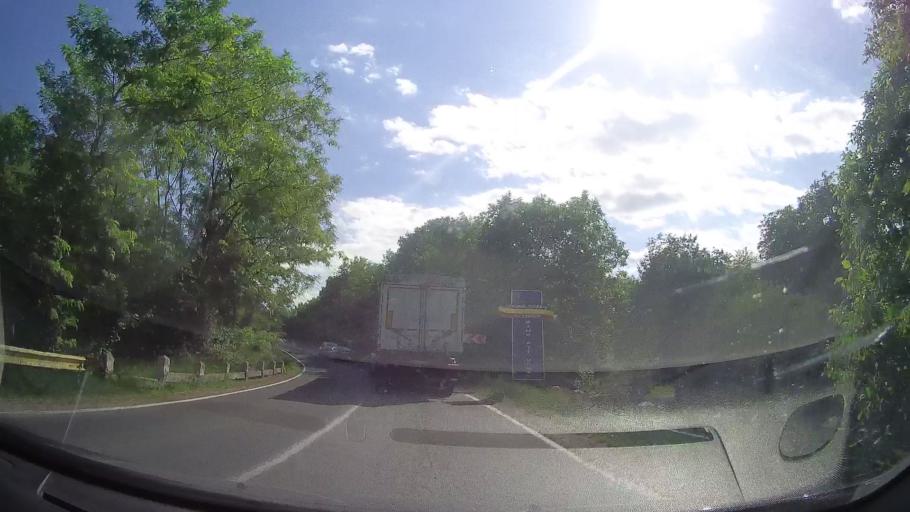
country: RO
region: Prahova
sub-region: Comuna Izvoarele
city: Homoraciu
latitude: 45.2493
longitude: 26.0244
